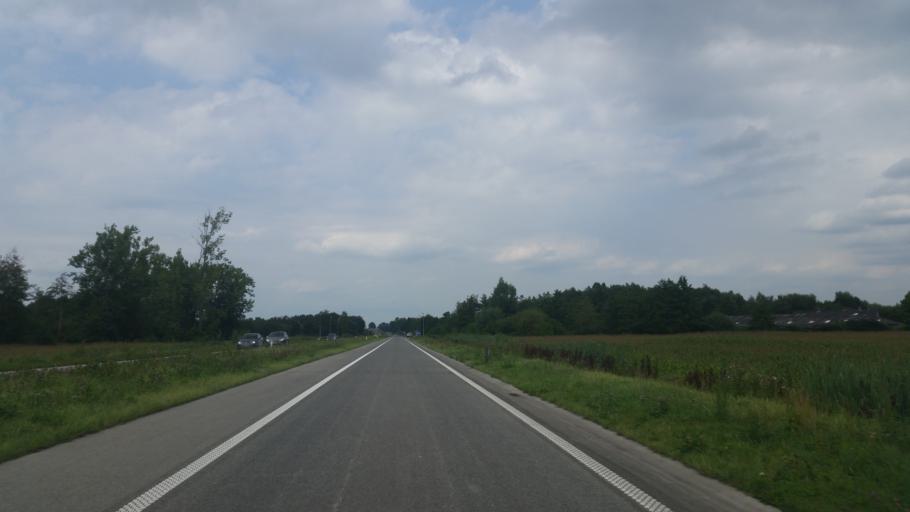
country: BE
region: Flanders
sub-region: Provincie Antwerpen
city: Geel
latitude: 51.1858
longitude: 4.9733
